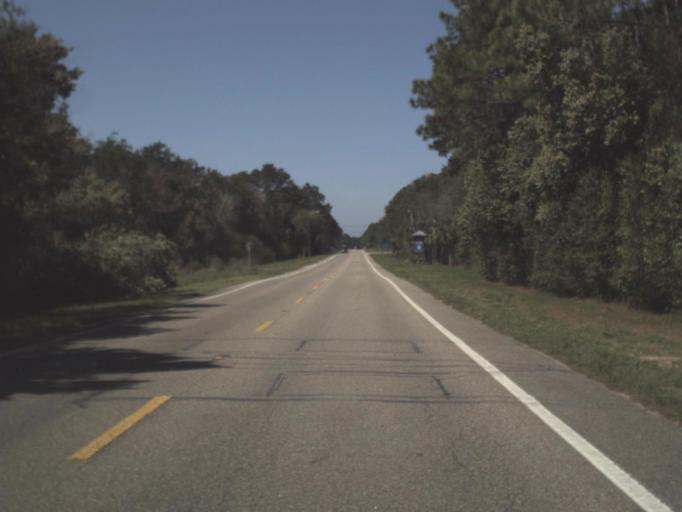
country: US
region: Florida
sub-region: Gulf County
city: Port Saint Joe
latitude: 29.7766
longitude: -85.2760
